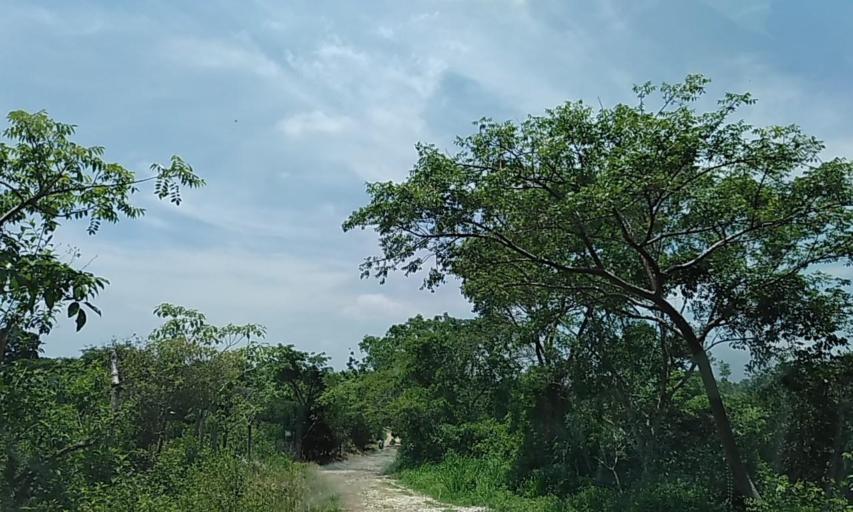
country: MX
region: Veracruz
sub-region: Emiliano Zapata
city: Dos Rios
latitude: 19.4414
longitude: -96.7592
